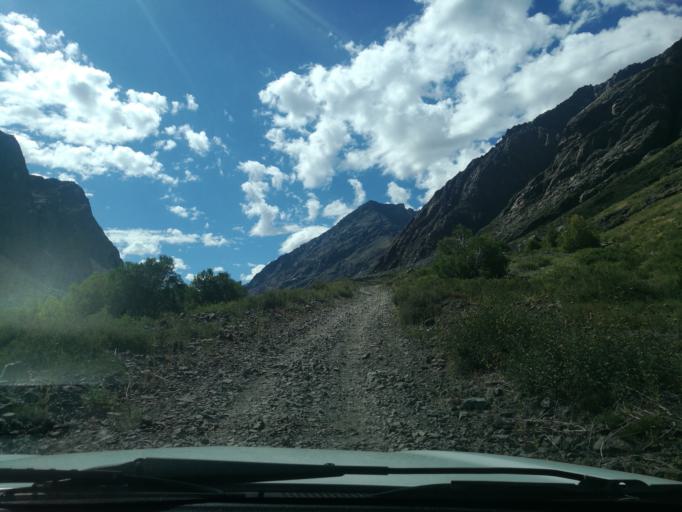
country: CL
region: O'Higgins
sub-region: Provincia de Cachapoal
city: Machali
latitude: -34.4039
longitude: -70.2530
